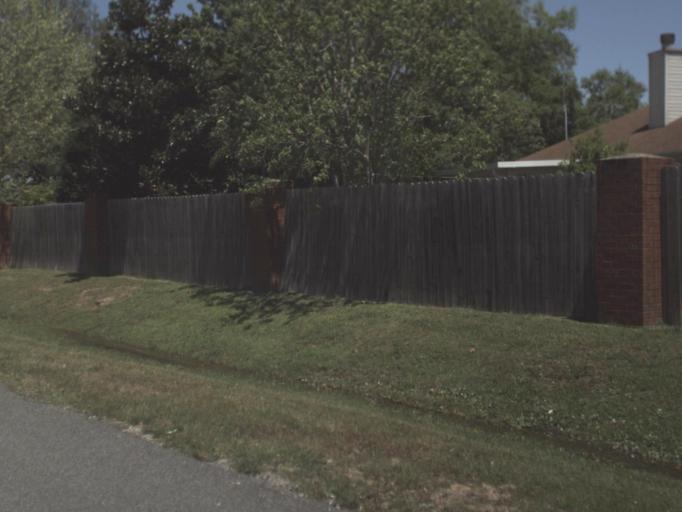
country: US
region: Florida
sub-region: Escambia County
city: Bellview
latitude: 30.4784
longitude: -87.3235
